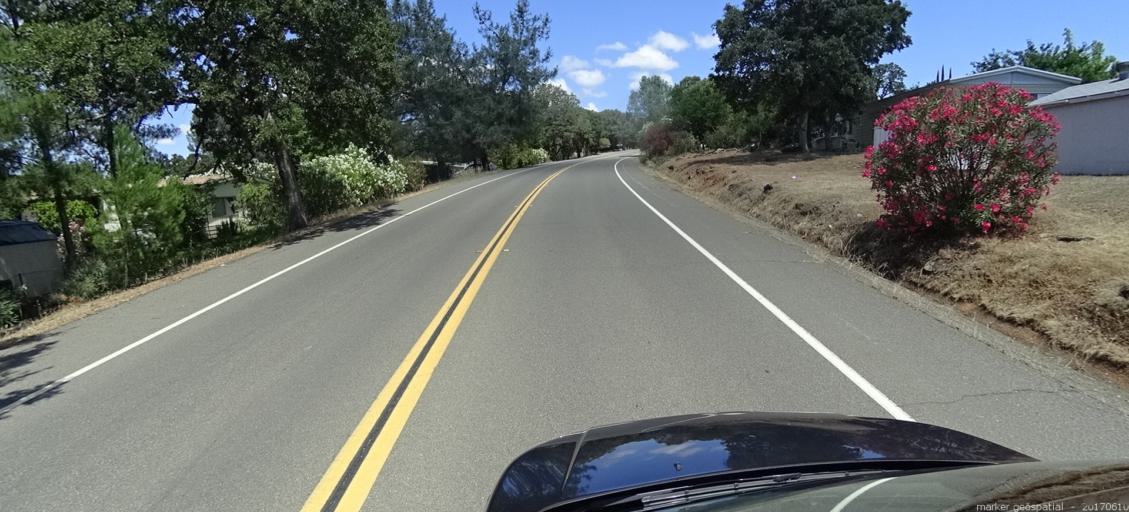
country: US
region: California
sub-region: Butte County
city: Oroville East
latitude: 39.5280
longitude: -121.4673
